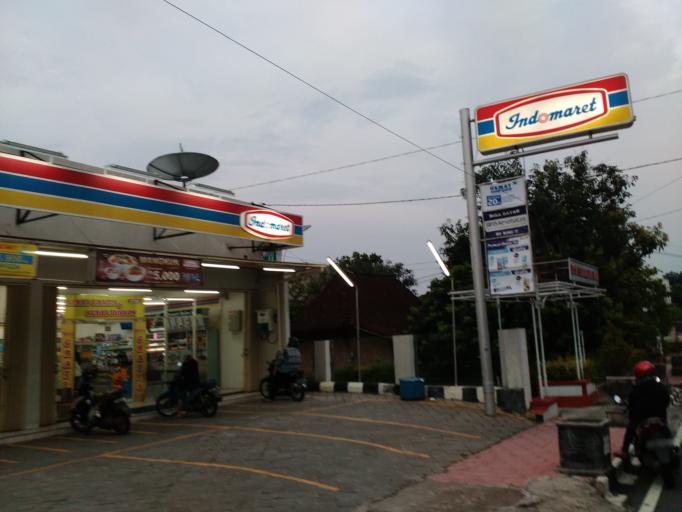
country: ID
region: Central Java
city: Boyolali
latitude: -7.5315
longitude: 110.5953
